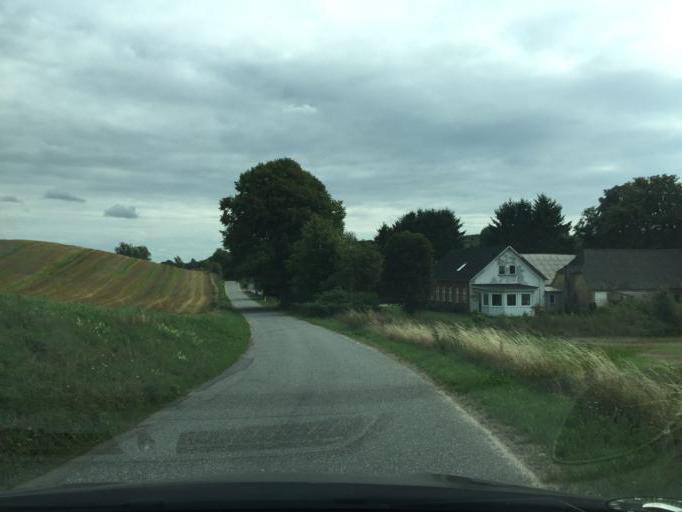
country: DK
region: South Denmark
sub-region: Assens Kommune
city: Vissenbjerg
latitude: 55.3523
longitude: 10.1197
